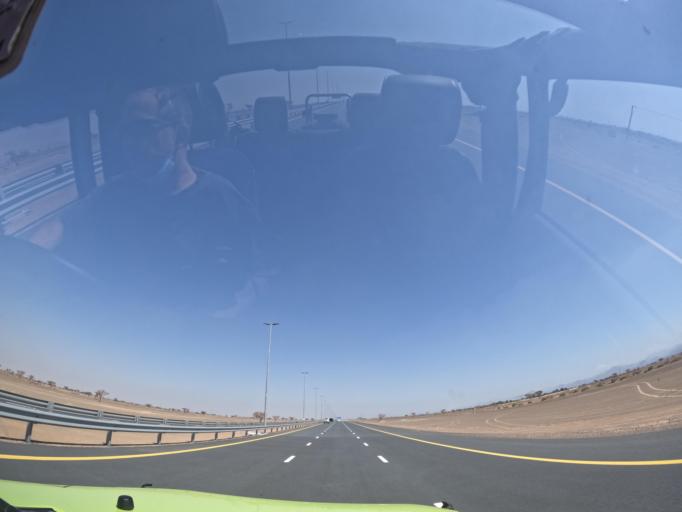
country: AE
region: Ash Shariqah
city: Adh Dhayd
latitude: 25.0877
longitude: 55.9195
